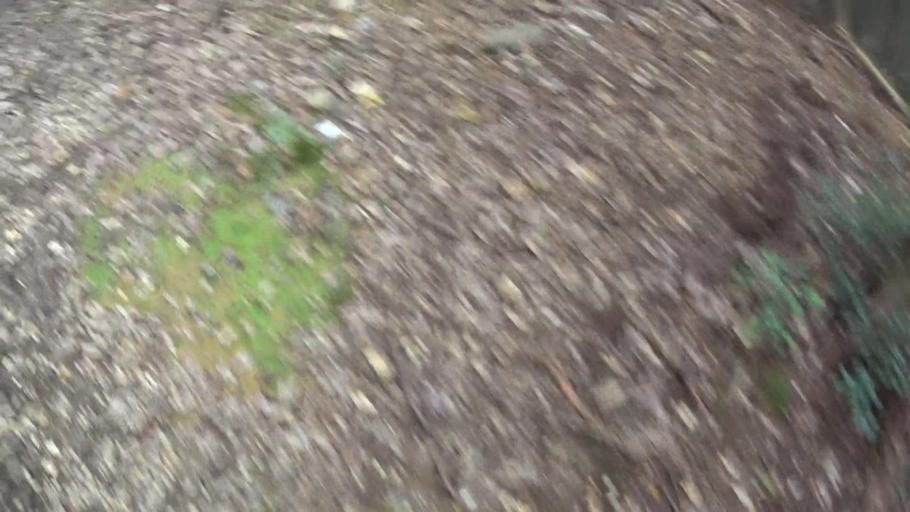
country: JP
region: Osaka
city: Kishiwada
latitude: 34.4972
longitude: 135.3298
